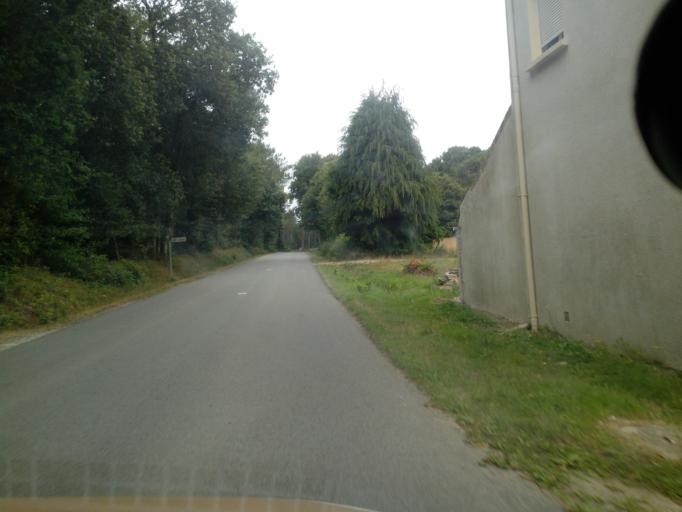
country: FR
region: Brittany
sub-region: Departement du Morbihan
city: Merlevenez
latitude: 47.7137
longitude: -3.2573
